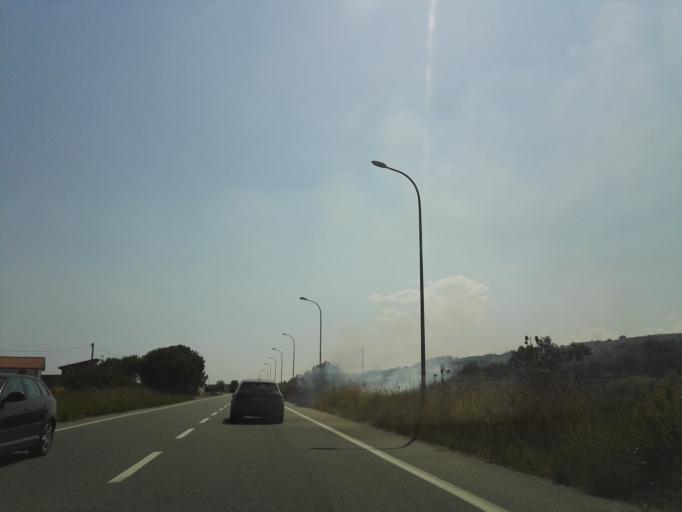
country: IT
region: Calabria
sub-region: Provincia di Reggio Calabria
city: Riace Marina
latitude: 38.4075
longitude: 16.5499
